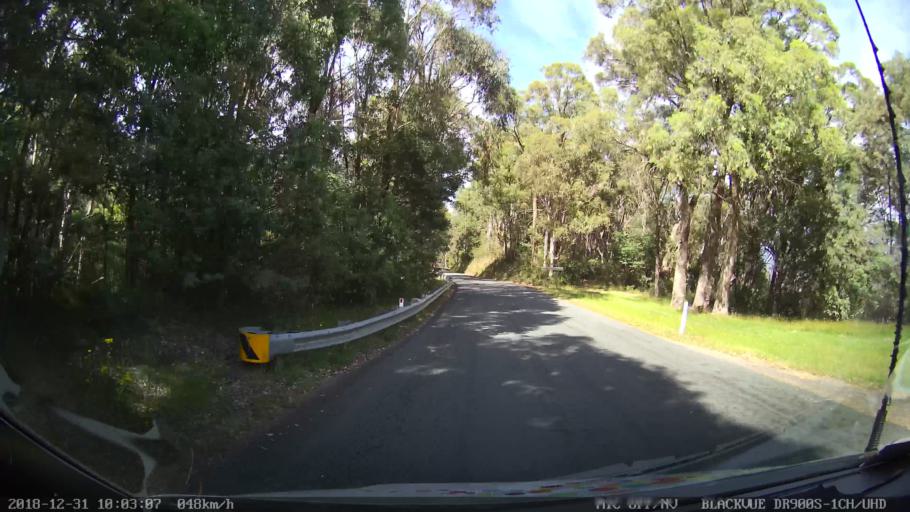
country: AU
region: New South Wales
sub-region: Snowy River
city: Jindabyne
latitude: -36.5313
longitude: 148.1935
